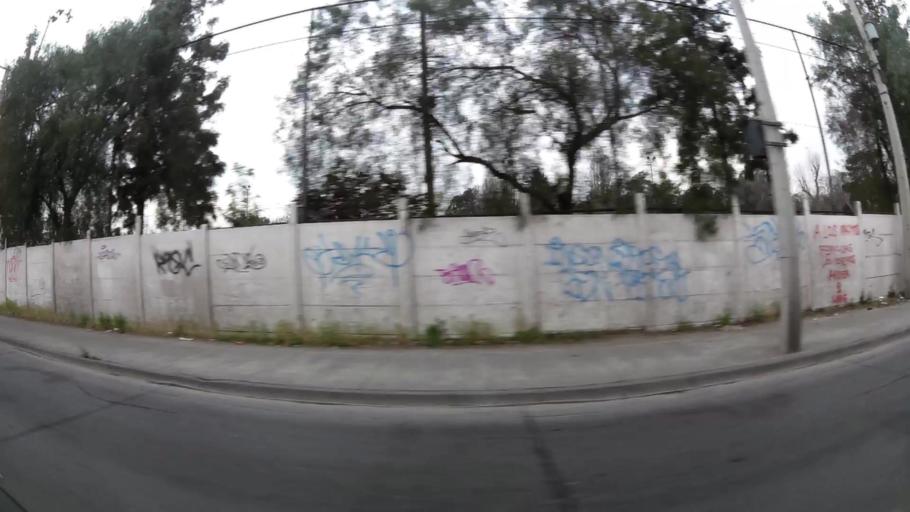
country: CL
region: Santiago Metropolitan
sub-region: Provincia de Santiago
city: Santiago
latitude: -33.4244
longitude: -70.6722
